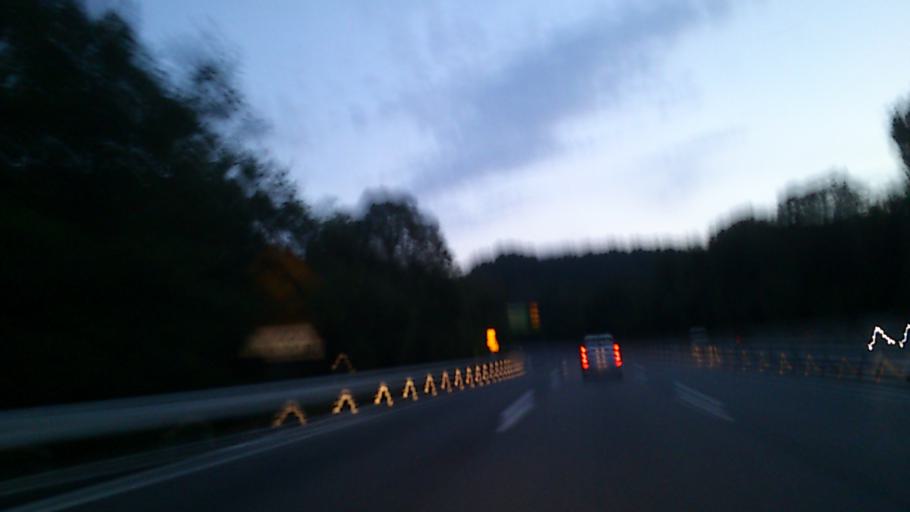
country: JP
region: Gifu
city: Tajimi
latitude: 35.3396
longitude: 137.0872
